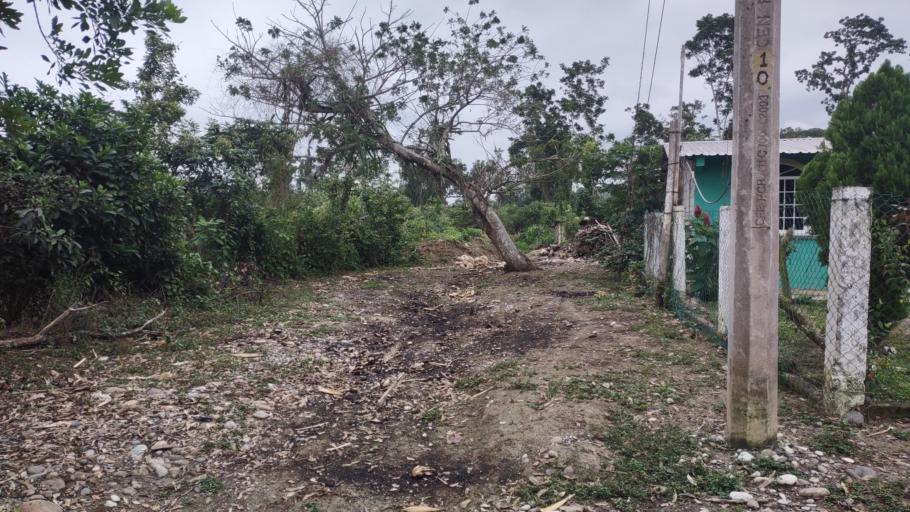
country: MX
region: Veracruz
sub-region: Coatzintla
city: Manuel Maria Contreras
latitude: 20.3992
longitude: -97.4375
